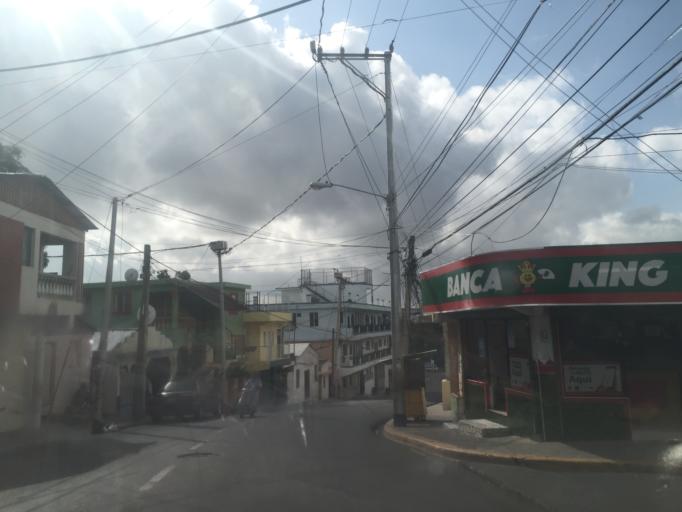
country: DO
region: Santiago
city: Santiago de los Caballeros
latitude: 19.4243
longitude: -70.7148
